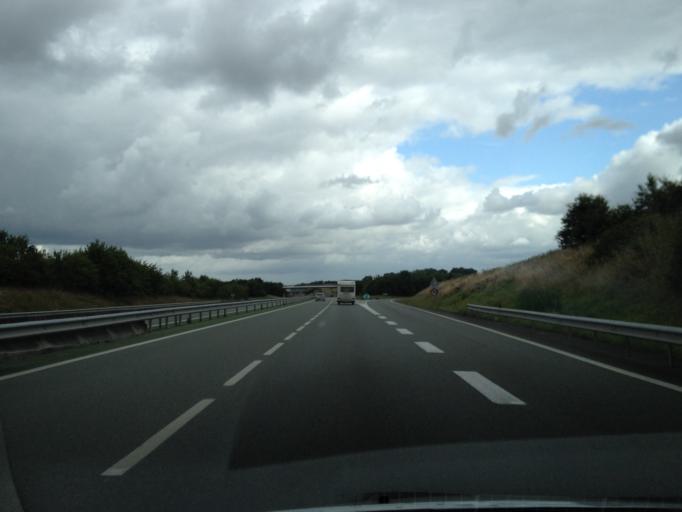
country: FR
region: Pays de la Loire
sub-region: Departement de Maine-et-Loire
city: Nuaille
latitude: 47.0829
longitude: -0.8246
